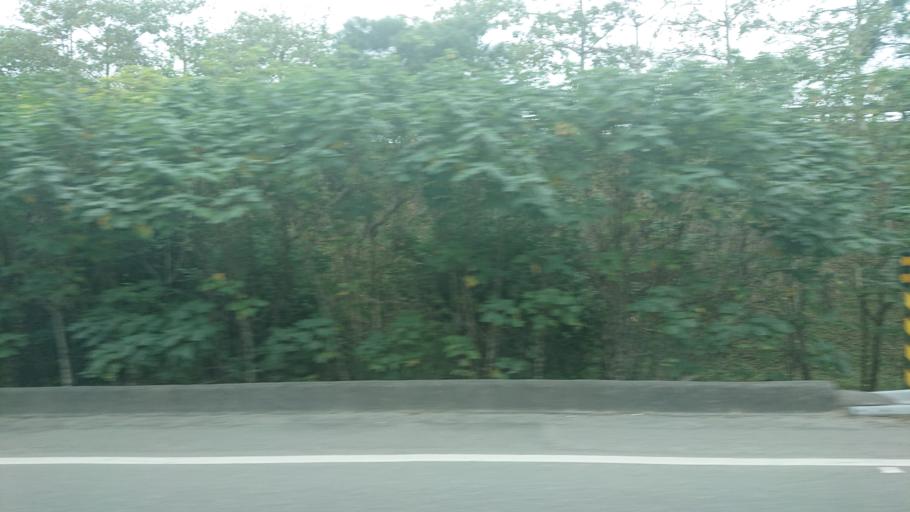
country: TW
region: Taiwan
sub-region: Taoyuan
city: Taoyuan
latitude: 24.9394
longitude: 121.3614
